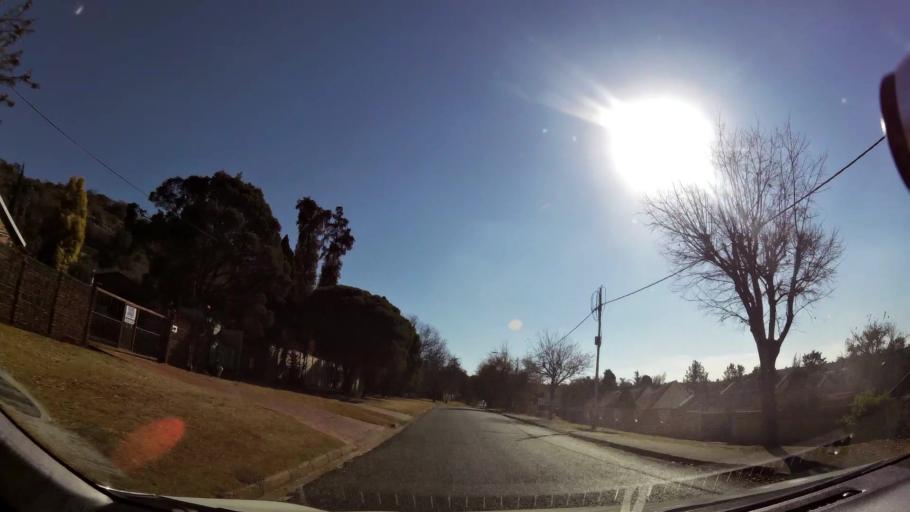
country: ZA
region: Gauteng
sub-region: City of Johannesburg Metropolitan Municipality
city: Johannesburg
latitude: -26.2807
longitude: 28.0045
